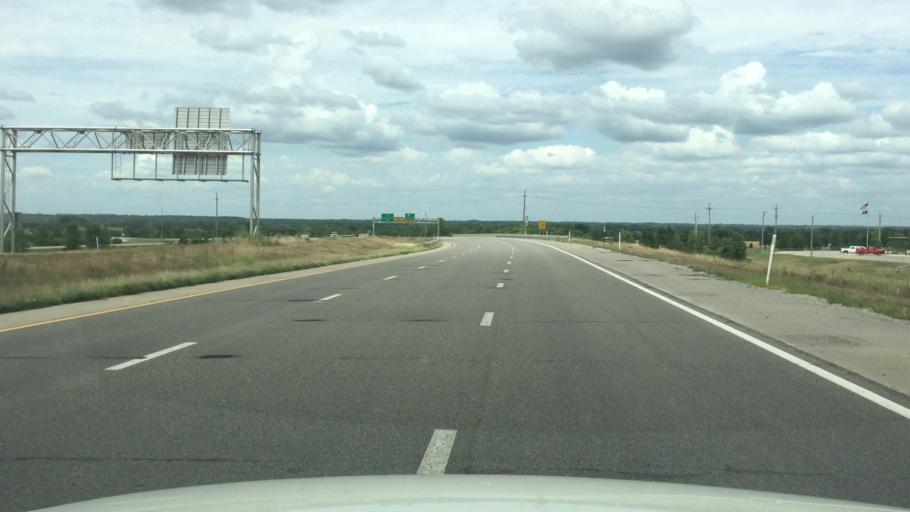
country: US
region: Kansas
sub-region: Shawnee County
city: Topeka
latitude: 39.0422
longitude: -95.6028
